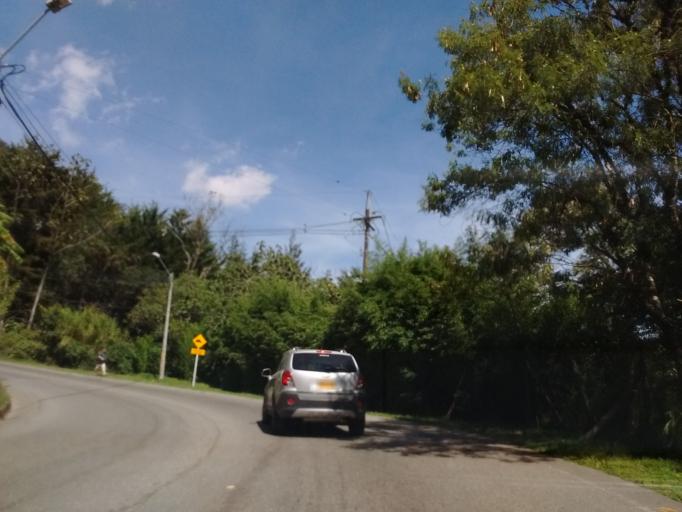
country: CO
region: Antioquia
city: Medellin
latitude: 6.2266
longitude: -75.5163
